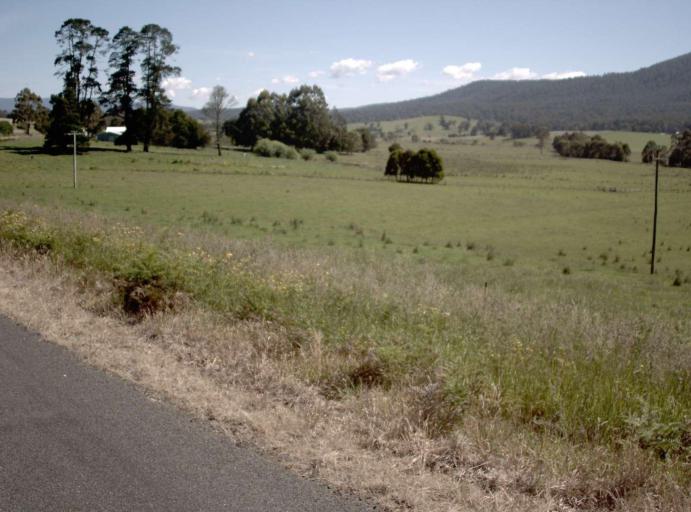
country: AU
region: New South Wales
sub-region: Bombala
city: Bombala
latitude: -37.1997
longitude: 148.7270
